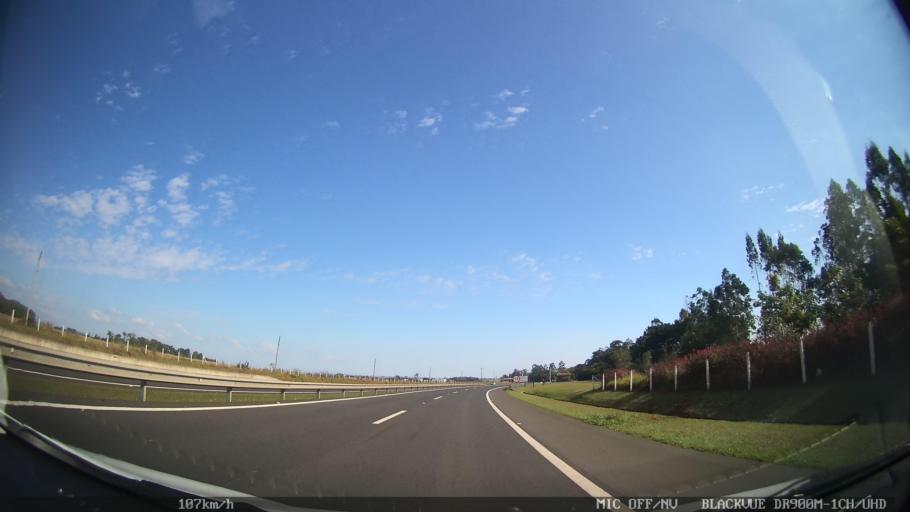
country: BR
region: Sao Paulo
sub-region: Iracemapolis
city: Iracemapolis
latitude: -22.6506
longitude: -47.5136
